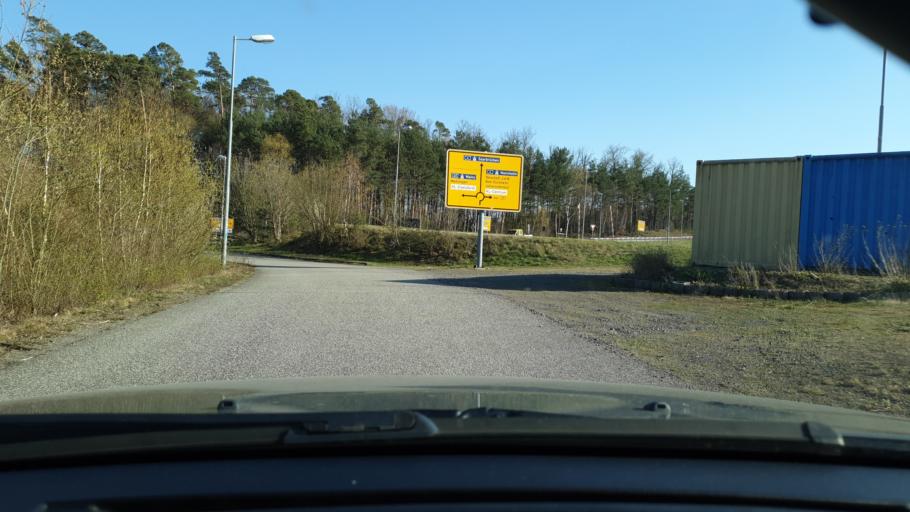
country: DE
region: Rheinland-Pfalz
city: Kaiserslautern
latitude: 49.4551
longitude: 7.8215
